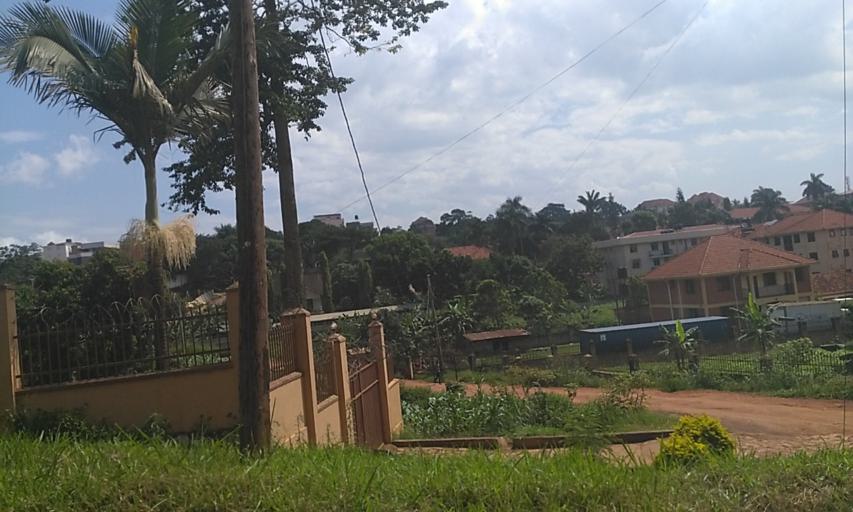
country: UG
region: Central Region
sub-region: Wakiso District
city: Kireka
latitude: 0.3474
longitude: 32.6124
